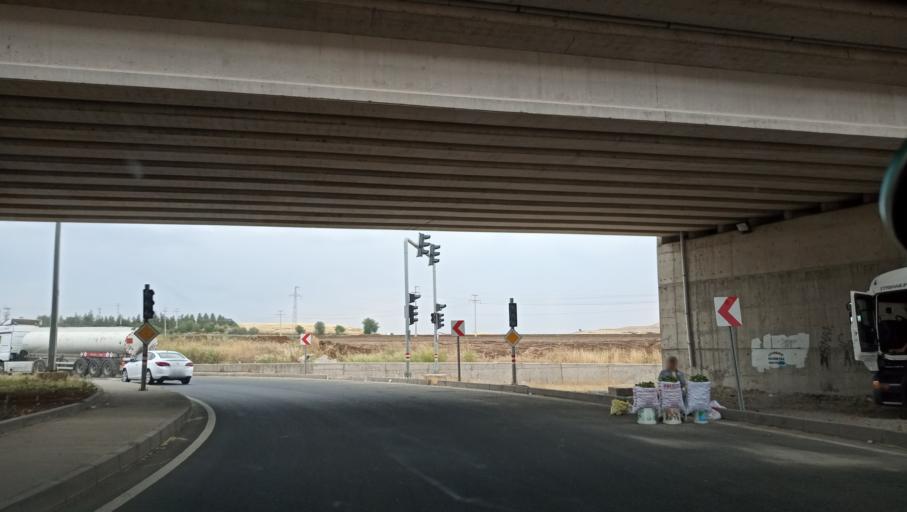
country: TR
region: Diyarbakir
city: Cinar
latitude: 37.8099
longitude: 40.3274
